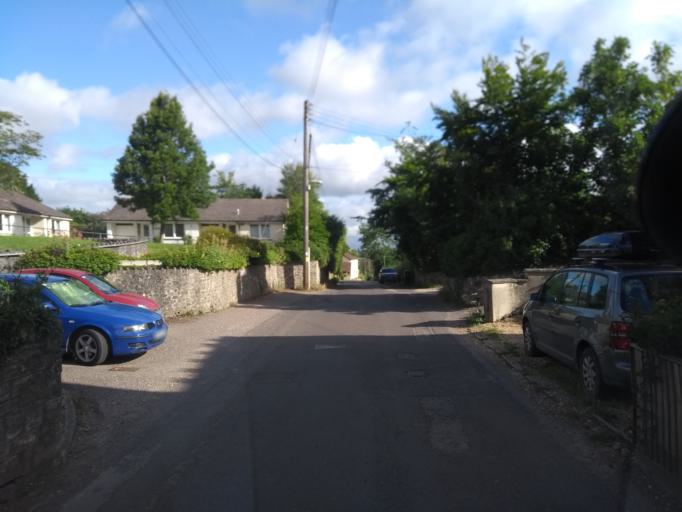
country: GB
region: England
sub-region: Somerset
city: Creech Saint Michael
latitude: 51.0241
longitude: -2.9730
